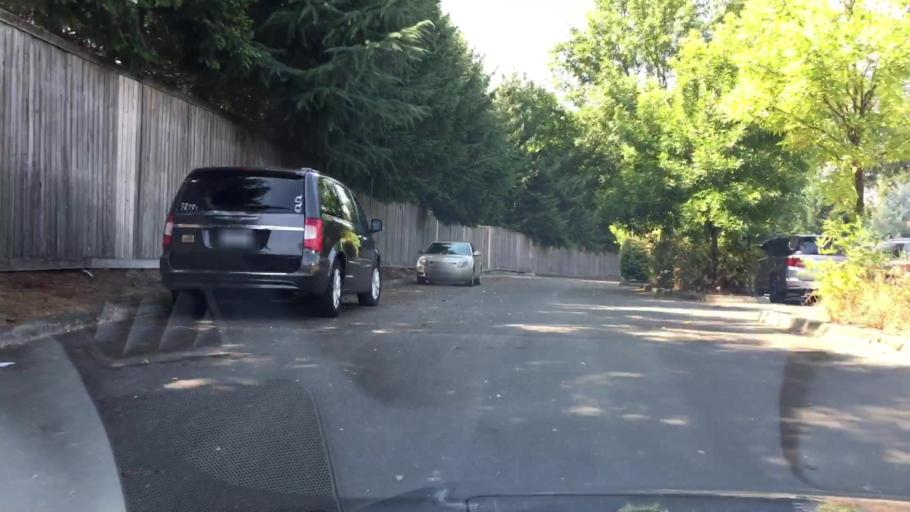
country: US
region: Washington
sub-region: Pierce County
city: Milton
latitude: 47.2707
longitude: -122.3120
